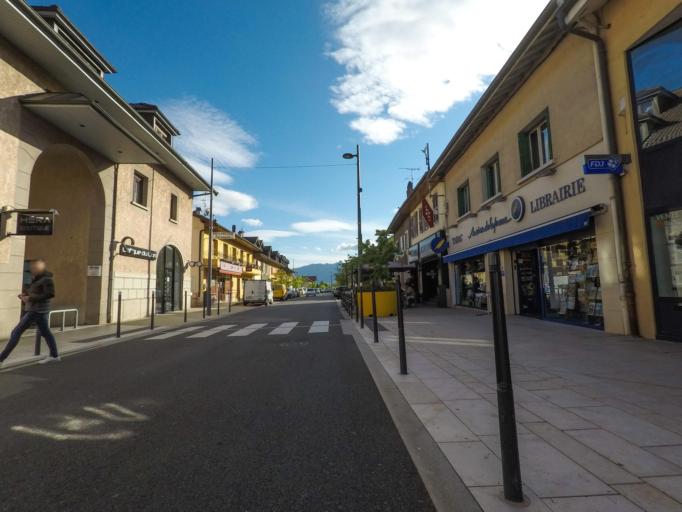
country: FR
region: Rhone-Alpes
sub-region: Departement de l'Ain
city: Saint-Genis-Pouilly
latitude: 46.2432
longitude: 6.0205
